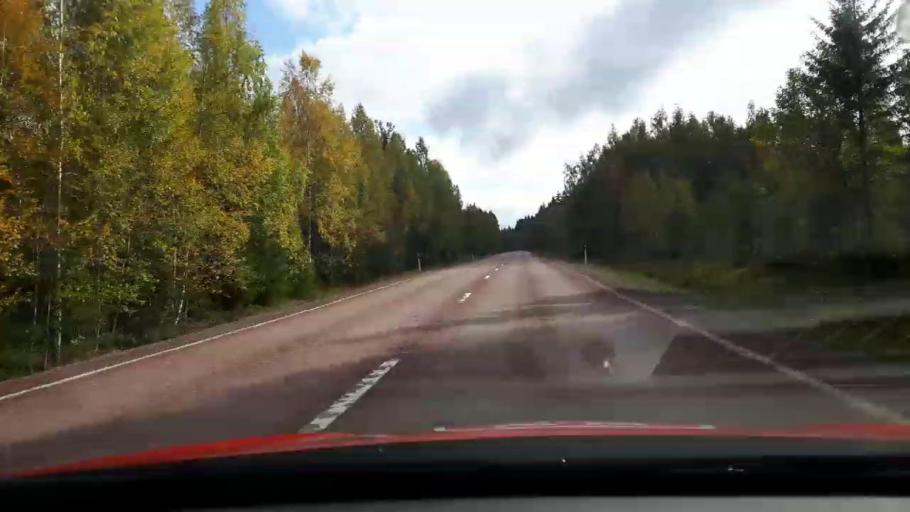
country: SE
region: Gaevleborg
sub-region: Ljusdals Kommun
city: Jaervsoe
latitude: 61.6411
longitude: 16.2315
